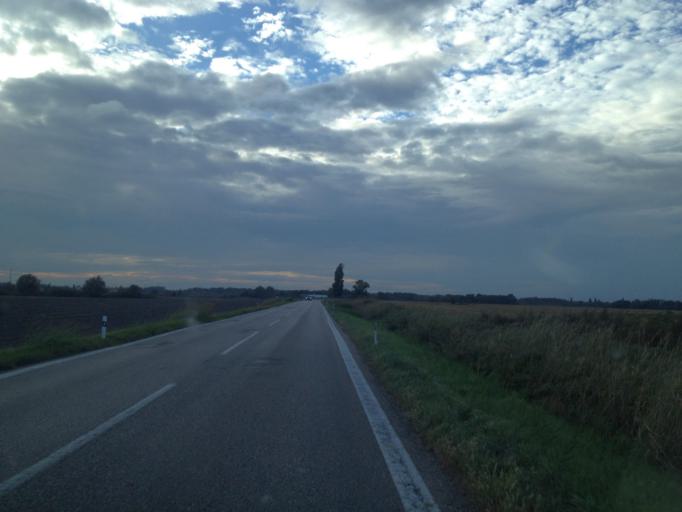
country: SK
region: Nitriansky
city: Komarno
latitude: 47.7628
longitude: 18.1803
